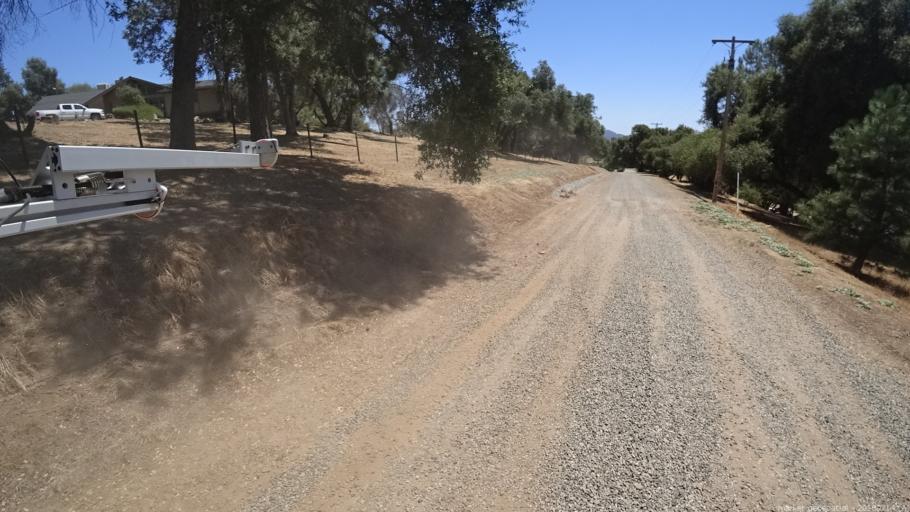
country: US
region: California
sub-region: Madera County
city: Ahwahnee
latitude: 37.4023
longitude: -119.7373
